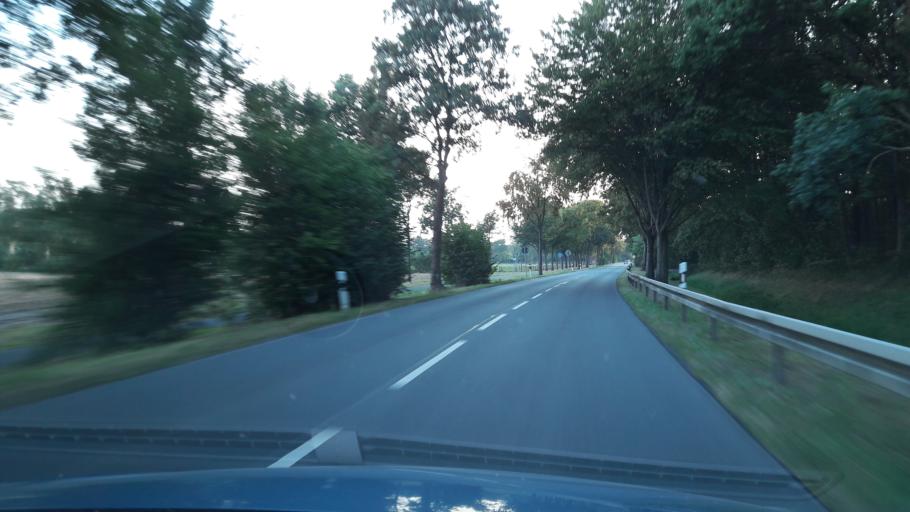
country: DE
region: North Rhine-Westphalia
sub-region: Regierungsbezirk Munster
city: Ennigerloh
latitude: 51.8161
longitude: 7.9522
